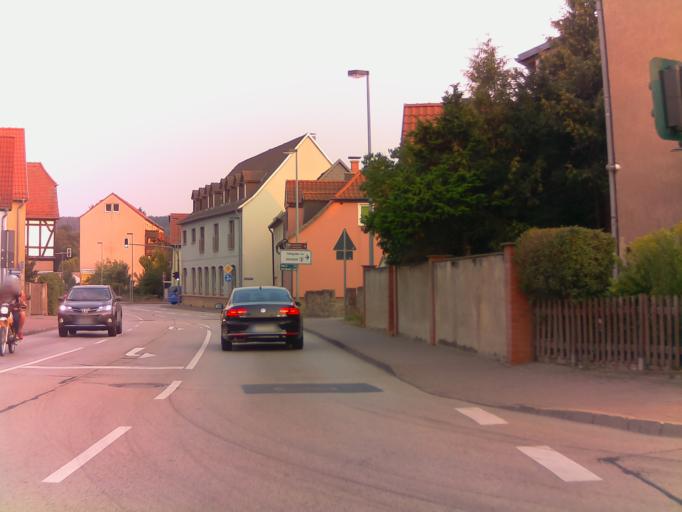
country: DE
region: Thuringia
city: Bad Berka
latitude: 50.9000
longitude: 11.2810
